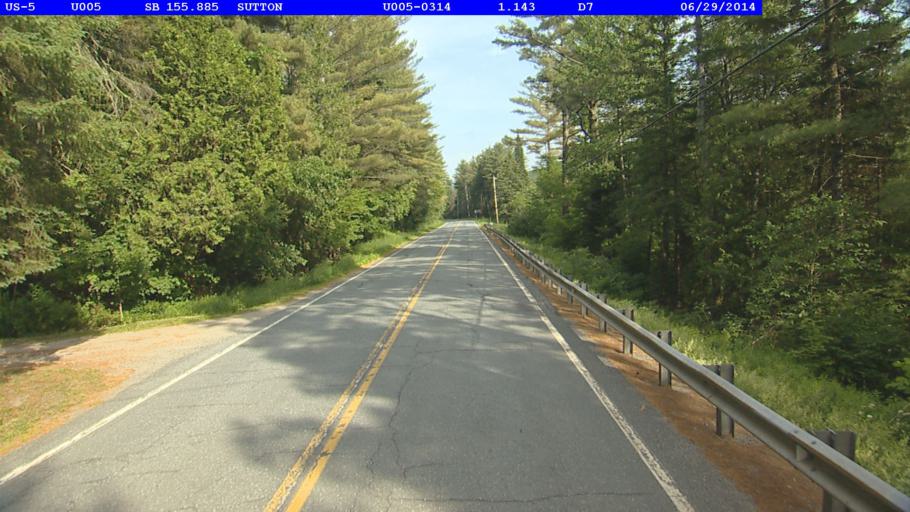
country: US
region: Vermont
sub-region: Caledonia County
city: Lyndonville
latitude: 44.6478
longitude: -72.0054
